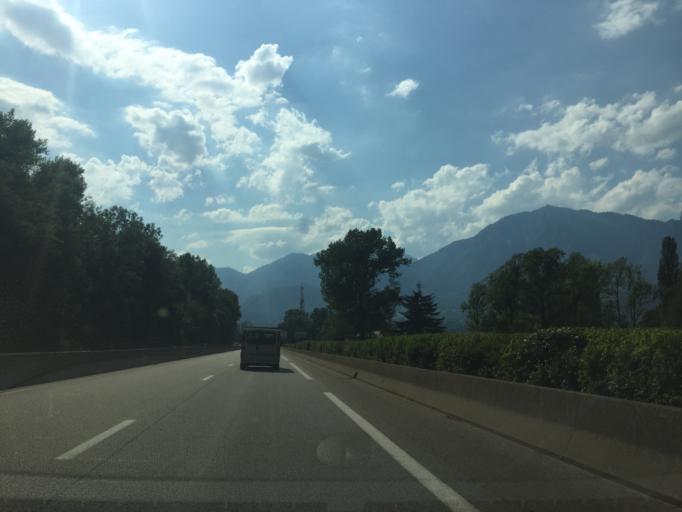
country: FR
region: Rhone-Alpes
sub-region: Departement de la Savoie
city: Albertville
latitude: 45.6629
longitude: 6.4026
